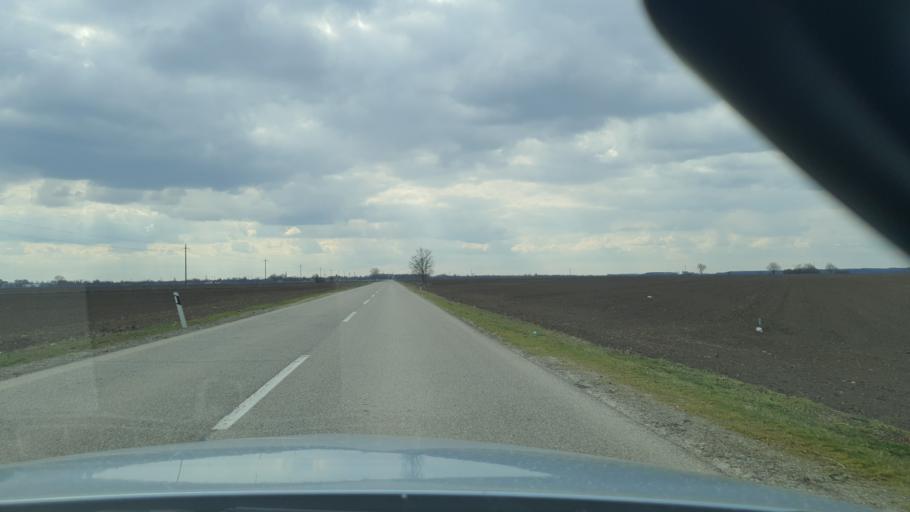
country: RS
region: Autonomna Pokrajina Vojvodina
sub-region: Juznobacki Okrug
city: Bac
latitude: 45.4332
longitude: 19.3110
